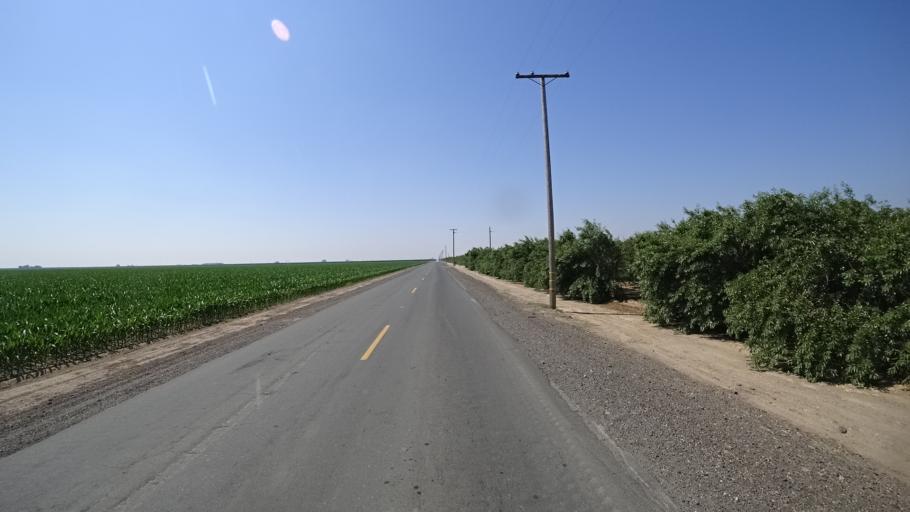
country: US
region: California
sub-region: Fresno County
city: Kingsburg
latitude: 36.4390
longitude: -119.5286
